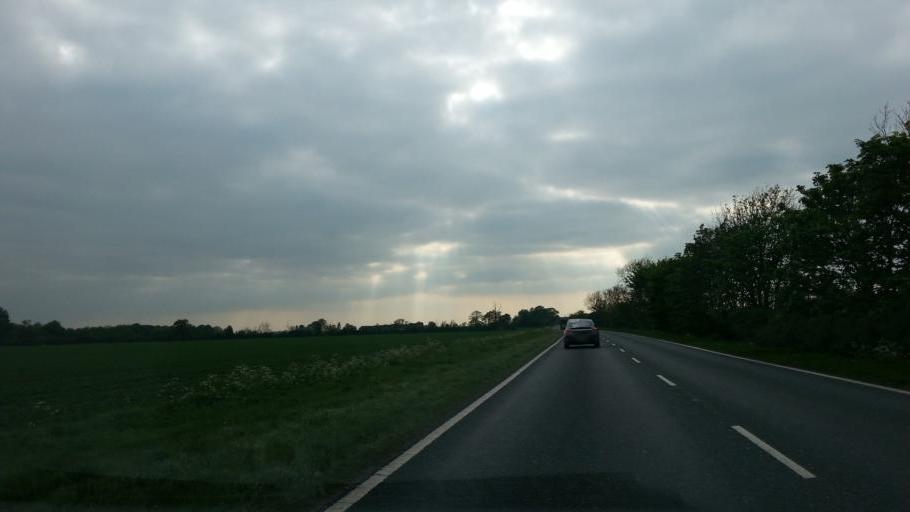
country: GB
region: England
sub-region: Lincolnshire
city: Navenby
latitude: 53.0692
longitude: -0.6482
